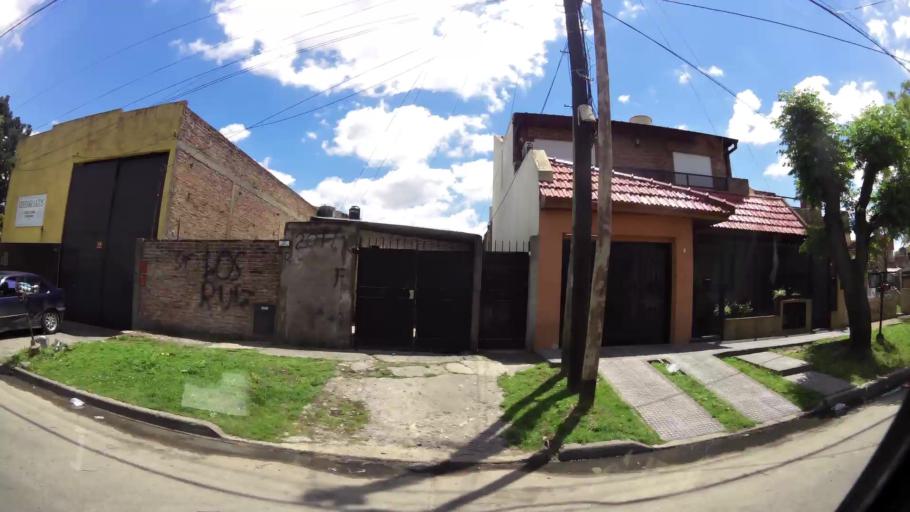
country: AR
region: Buenos Aires
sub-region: Partido de Lanus
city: Lanus
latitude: -34.7061
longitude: -58.4272
